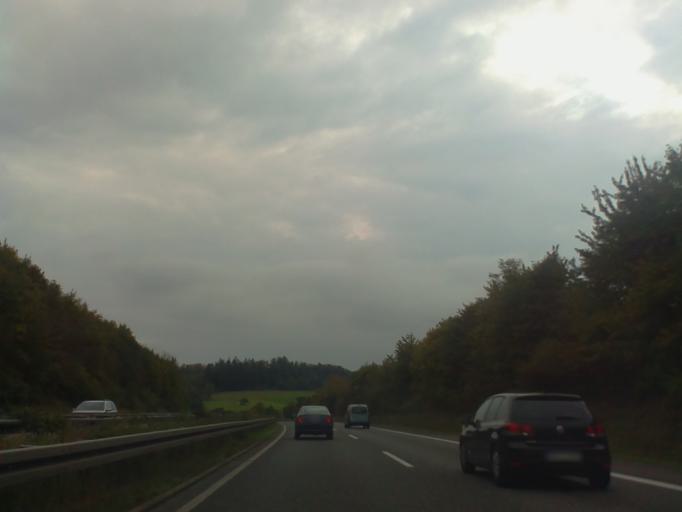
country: DE
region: Hesse
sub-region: Regierungsbezirk Darmstadt
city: Schluchtern
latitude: 50.3658
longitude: 9.5028
